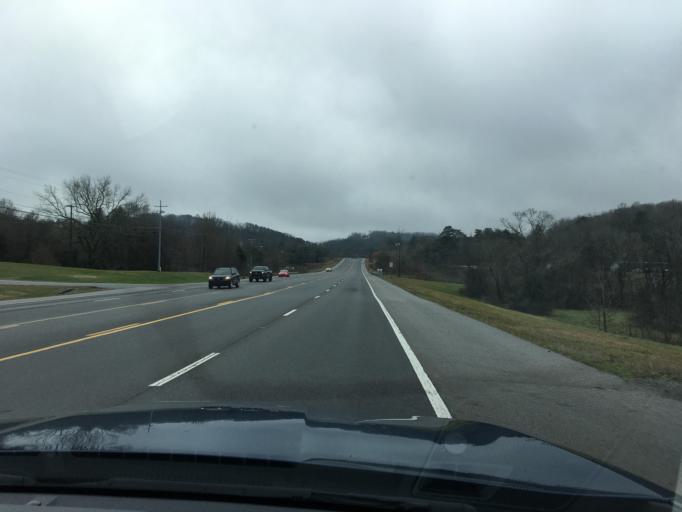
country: US
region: Tennessee
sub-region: McMinn County
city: Athens
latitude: 35.4221
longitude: -84.5840
